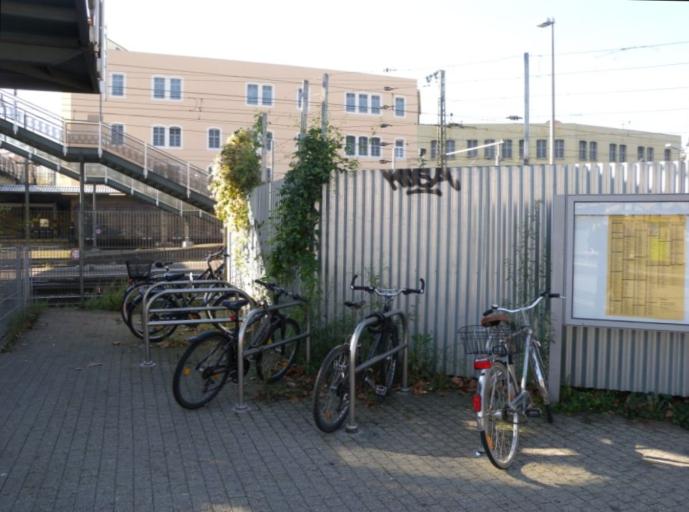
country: DE
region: Baden-Wuerttemberg
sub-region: Regierungsbezirk Stuttgart
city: Ludwigsburg
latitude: 48.8911
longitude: 9.1866
